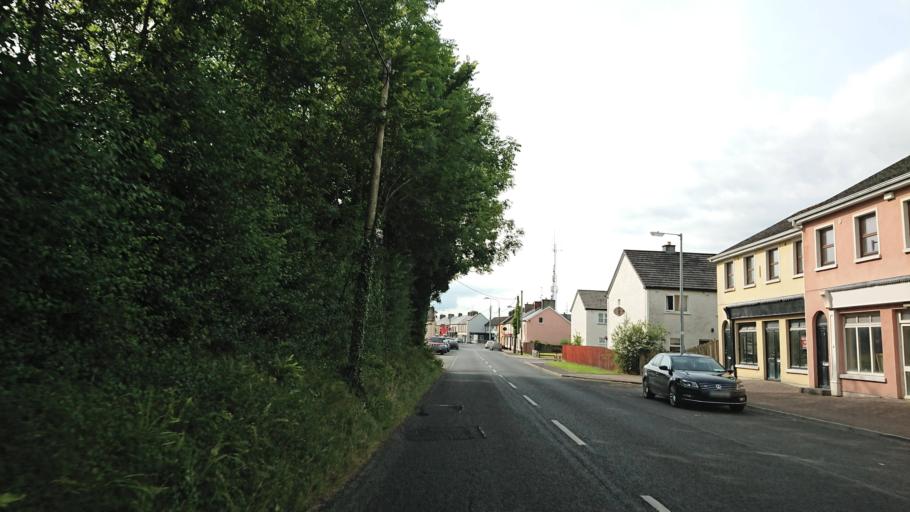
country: GB
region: Northern Ireland
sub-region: Fermanagh District
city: Enniskillen
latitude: 54.2905
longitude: -7.8737
